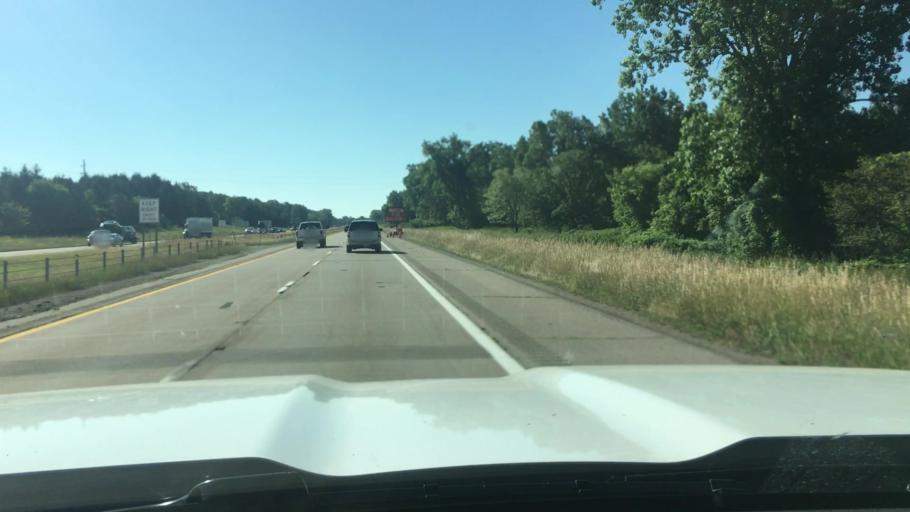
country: US
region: Michigan
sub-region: Ionia County
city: Portland
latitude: 42.8560
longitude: -84.8691
